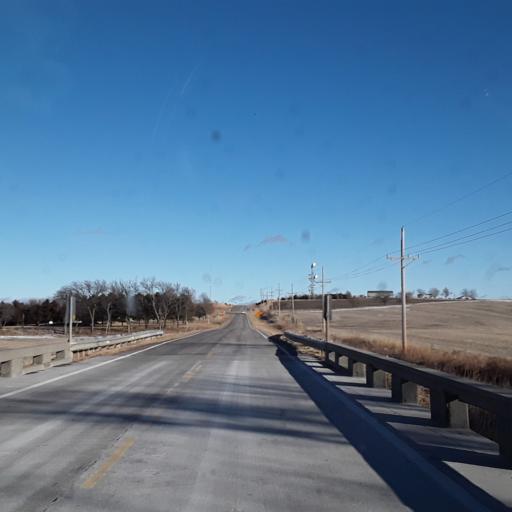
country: US
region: Kansas
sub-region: Cloud County
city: Concordia
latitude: 39.5666
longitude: -97.7134
